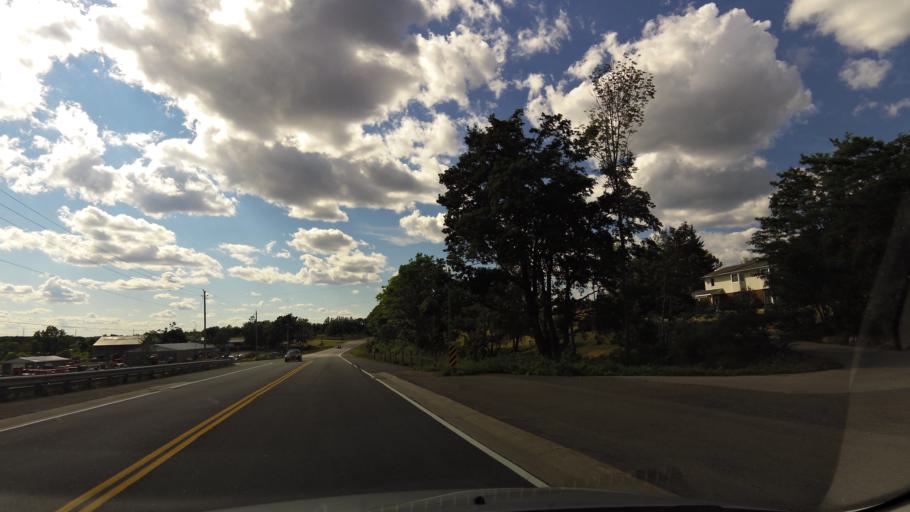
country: CA
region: Ontario
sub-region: Wellington County
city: Guelph
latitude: 43.4312
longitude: -80.0935
